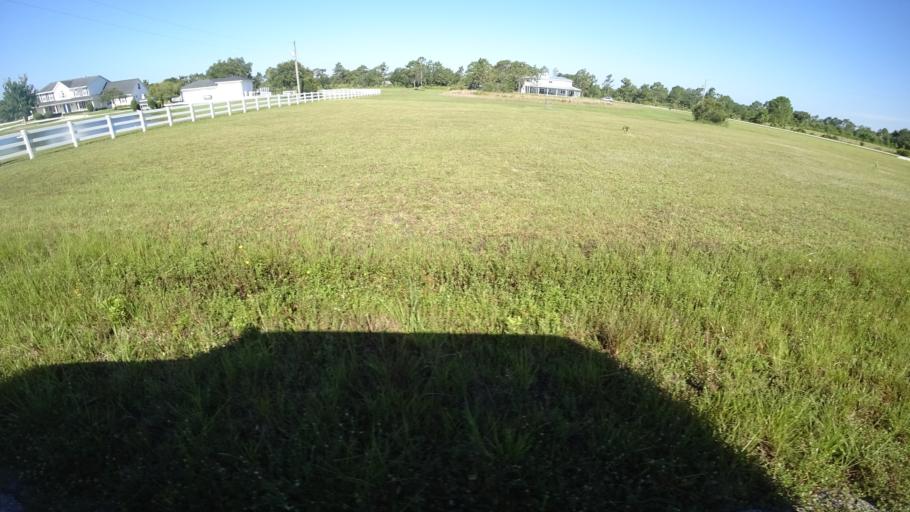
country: US
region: Florida
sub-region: Sarasota County
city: The Meadows
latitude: 27.4122
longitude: -82.3121
